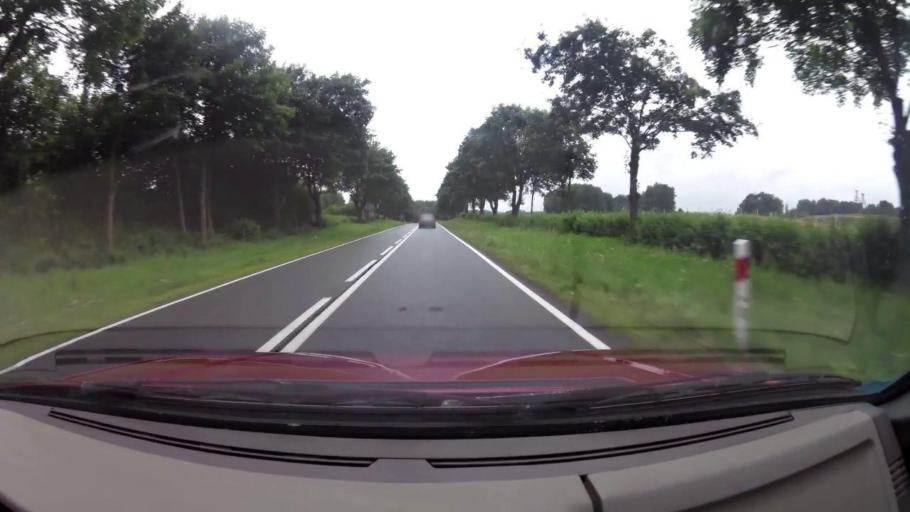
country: PL
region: West Pomeranian Voivodeship
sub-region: Powiat stargardzki
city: Chociwel
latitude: 53.4506
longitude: 15.3166
